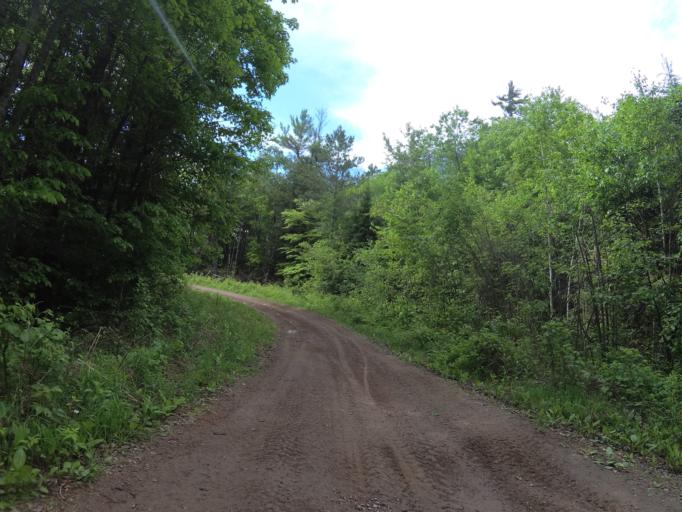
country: CA
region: Ontario
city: Renfrew
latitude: 45.1130
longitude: -76.8621
